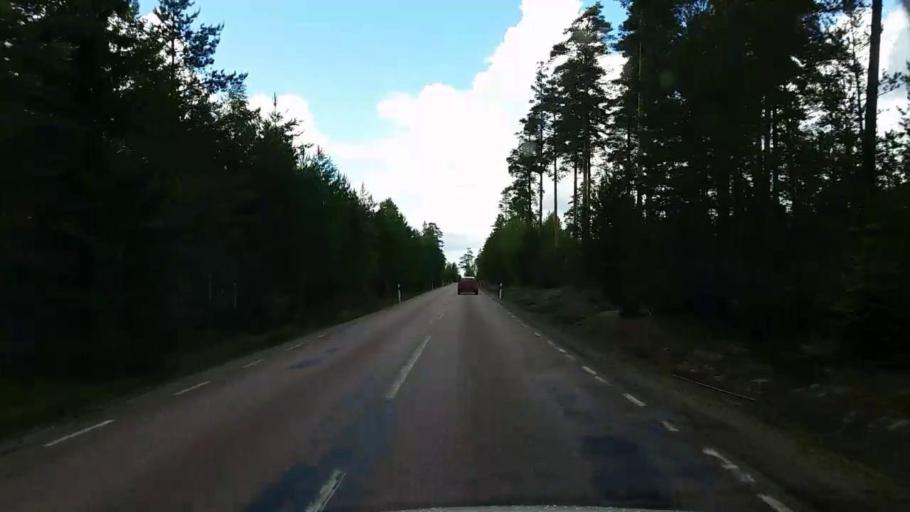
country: SE
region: Vaestmanland
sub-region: Fagersta Kommun
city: Fagersta
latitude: 59.8642
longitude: 15.8422
